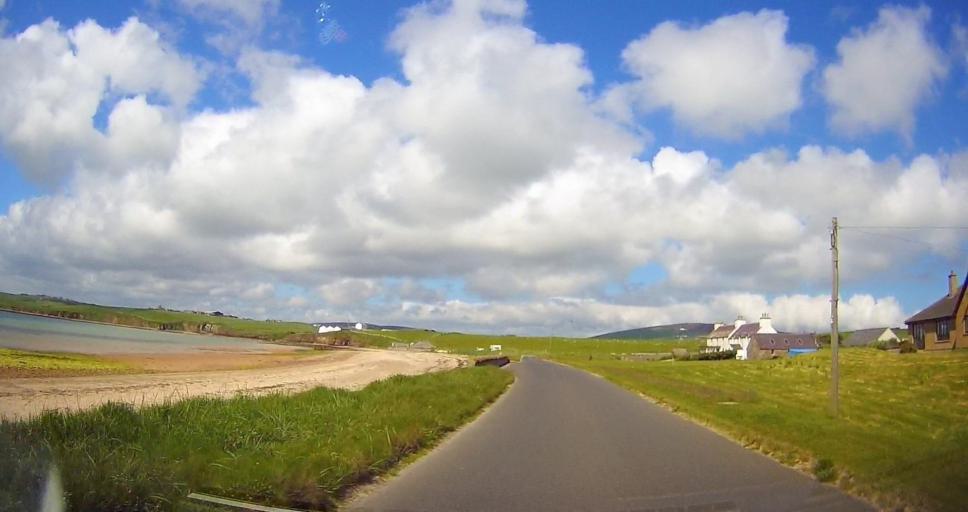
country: GB
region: Scotland
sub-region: Orkney Islands
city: Orkney
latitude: 58.9615
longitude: -2.9722
